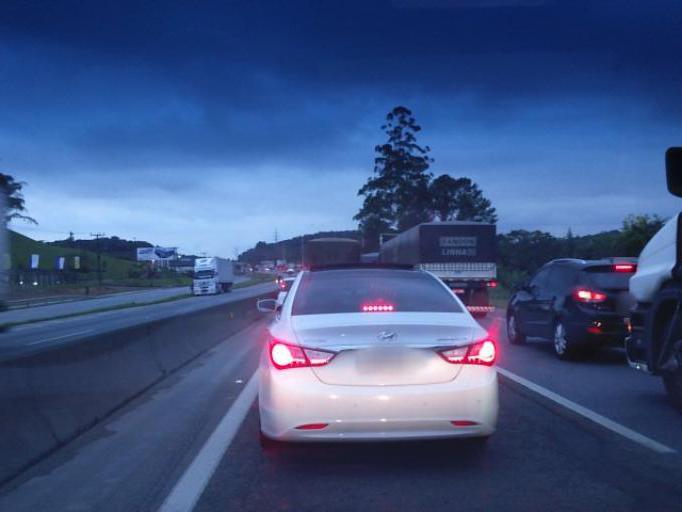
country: BR
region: Santa Catarina
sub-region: Joinville
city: Joinville
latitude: -26.3611
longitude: -48.8589
